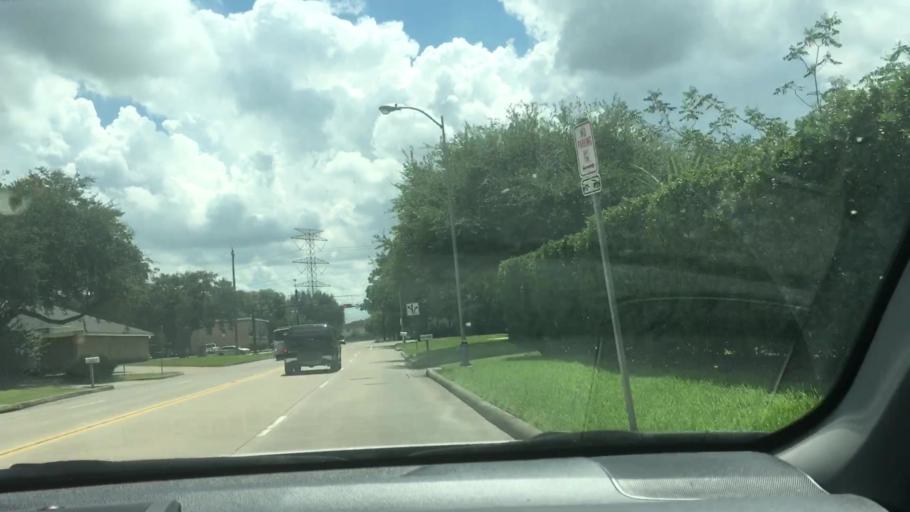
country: US
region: Texas
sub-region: Fort Bend County
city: Missouri City
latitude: 29.6112
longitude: -95.5441
